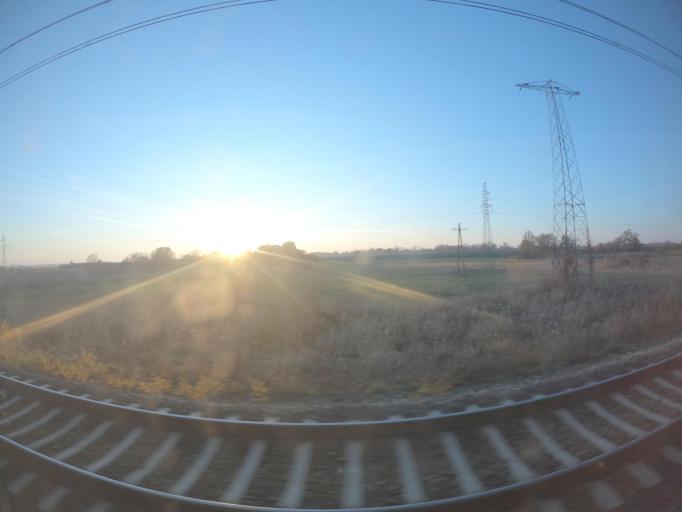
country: PL
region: Lubusz
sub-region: Powiat gorzowski
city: Kostrzyn nad Odra
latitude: 52.5676
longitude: 14.6461
